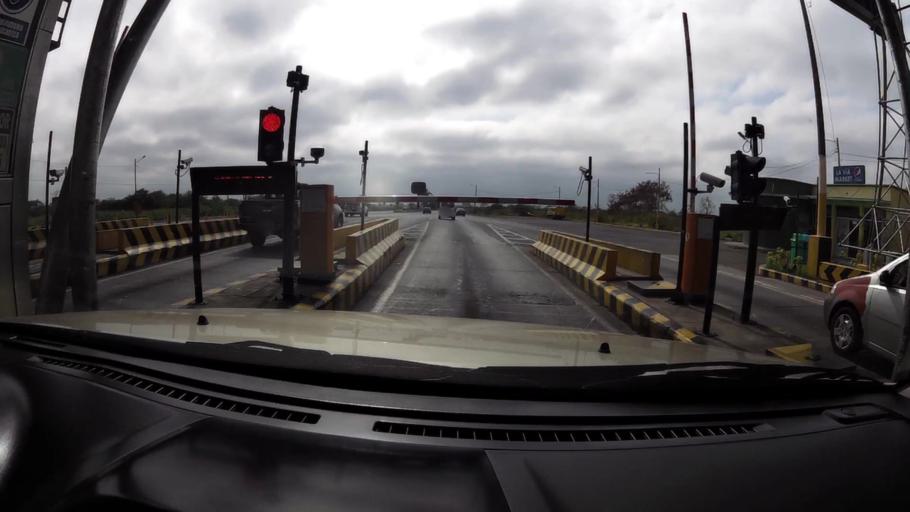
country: EC
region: Guayas
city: Eloy Alfaro
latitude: -2.2023
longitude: -79.7535
